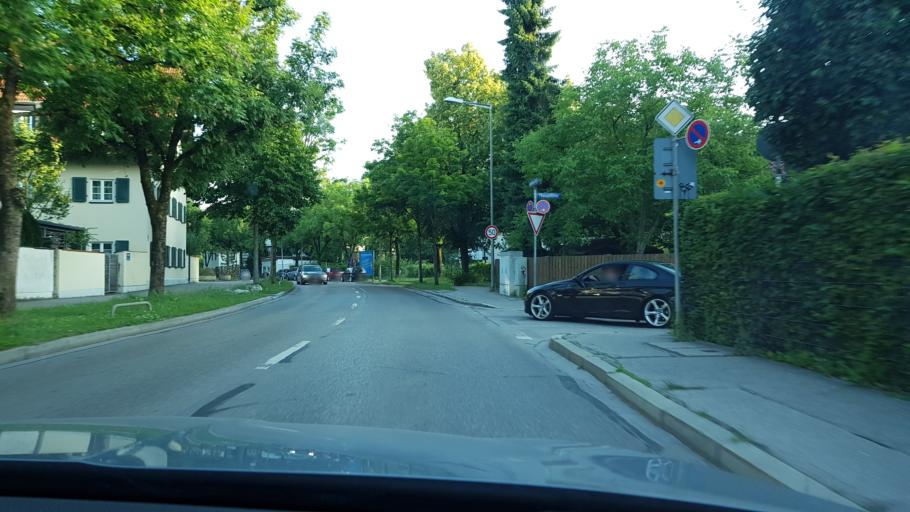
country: DE
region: Bavaria
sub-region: Upper Bavaria
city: Bogenhausen
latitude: 48.1702
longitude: 11.6245
